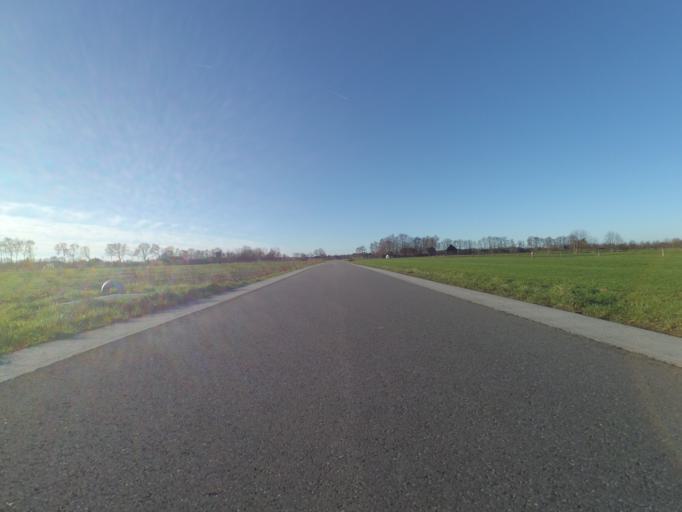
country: NL
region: Gelderland
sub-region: Gemeente Putten
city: Putten
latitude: 52.2461
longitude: 5.5716
